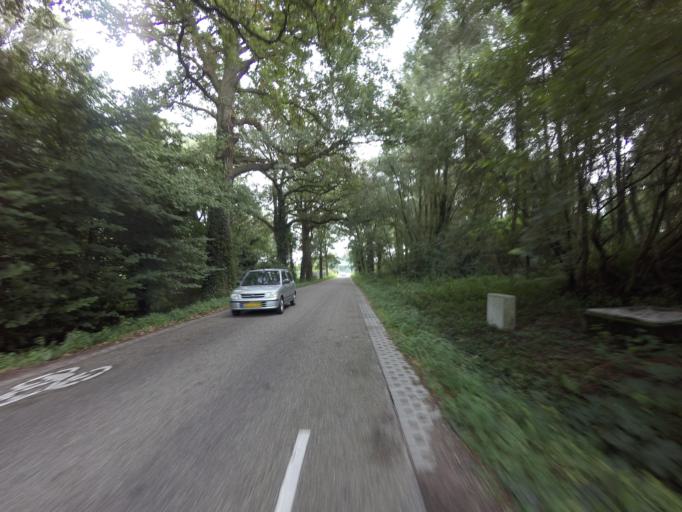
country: NL
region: Overijssel
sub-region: Gemeente Hengelo
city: Hengelo
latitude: 52.2882
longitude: 6.7970
